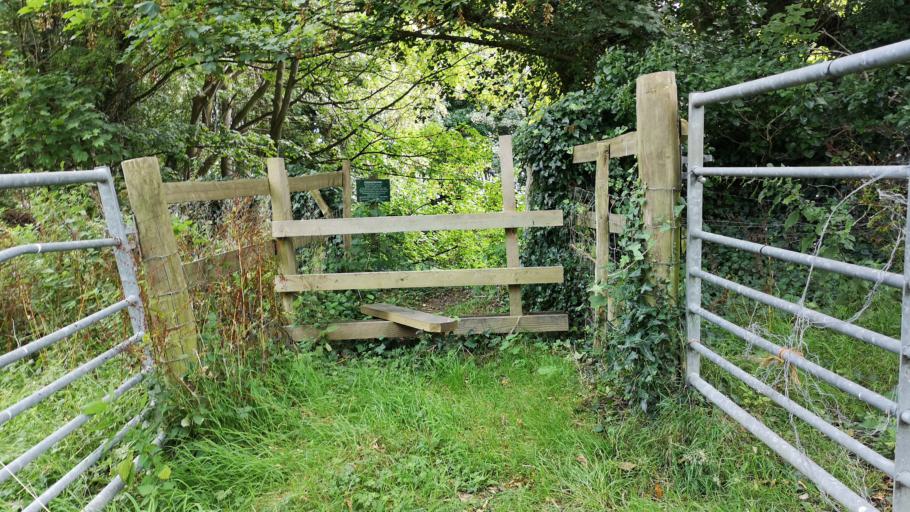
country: GB
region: England
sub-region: Isle of Wight
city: Ventnor
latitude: 50.5889
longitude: -1.2400
